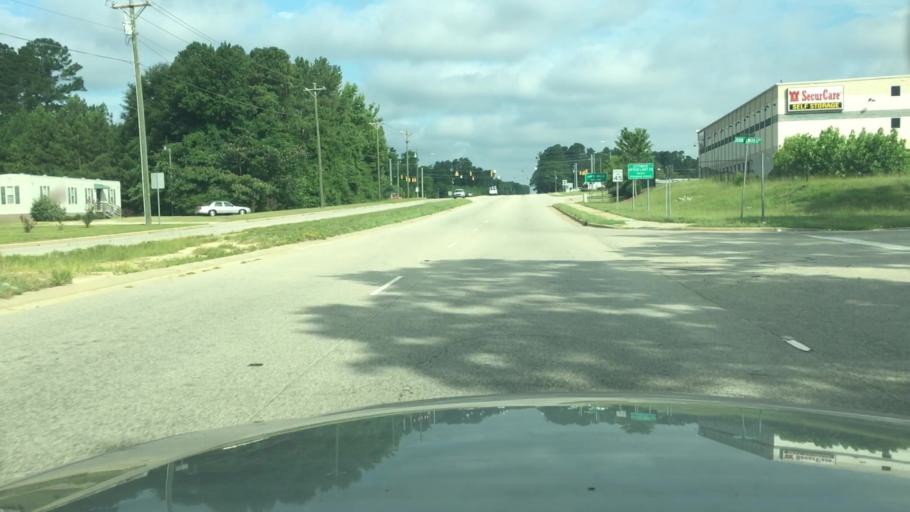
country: US
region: North Carolina
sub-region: Cumberland County
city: Hope Mills
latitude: 34.9940
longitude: -78.9653
